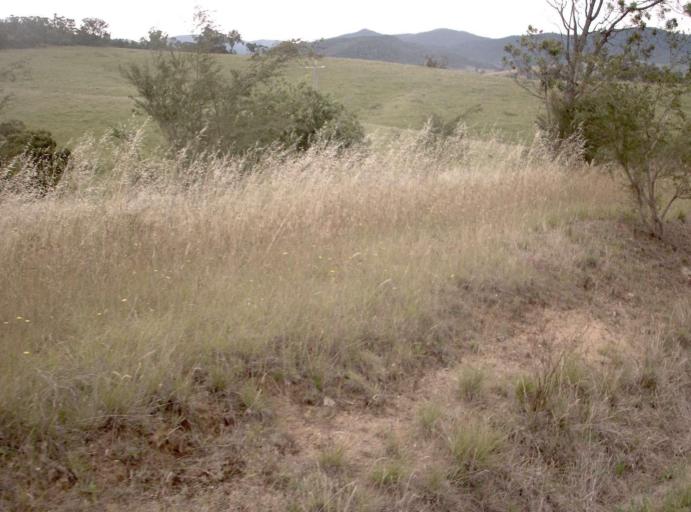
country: AU
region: Victoria
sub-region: East Gippsland
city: Bairnsdale
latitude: -37.4724
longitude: 147.2314
